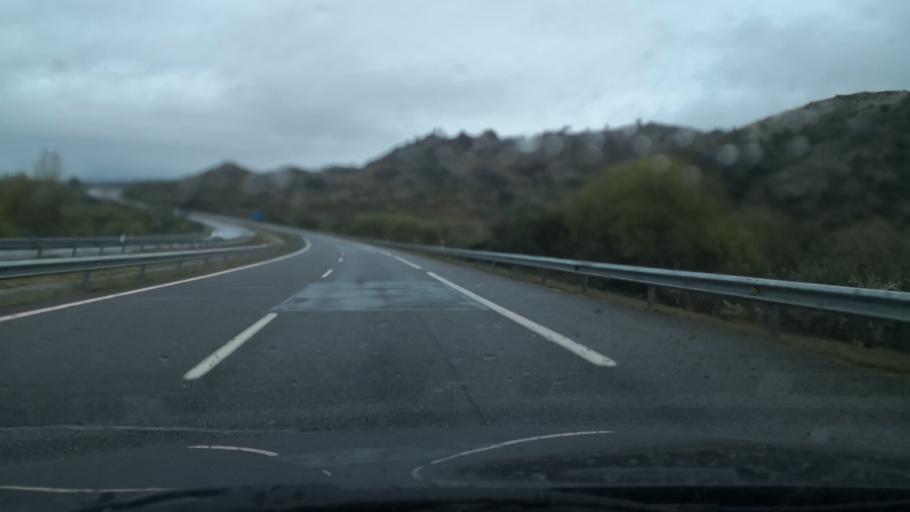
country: ES
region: Galicia
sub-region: Provincia de Ourense
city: Verin
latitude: 41.9203
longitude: -7.4133
